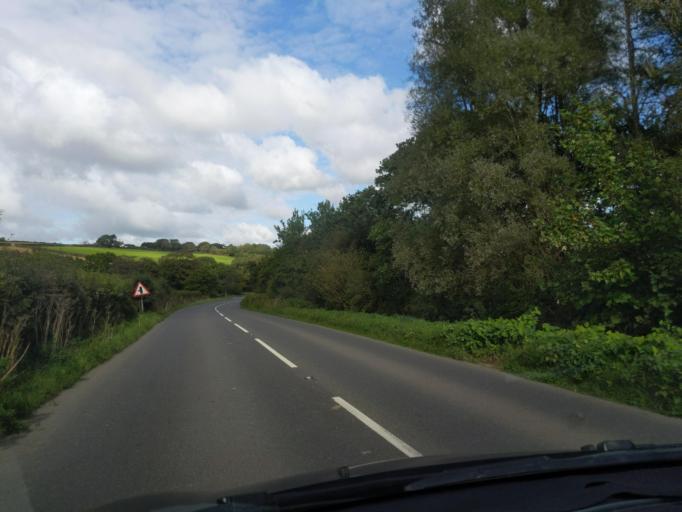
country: GB
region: England
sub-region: Devon
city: Holsworthy
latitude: 50.8678
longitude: -4.3225
